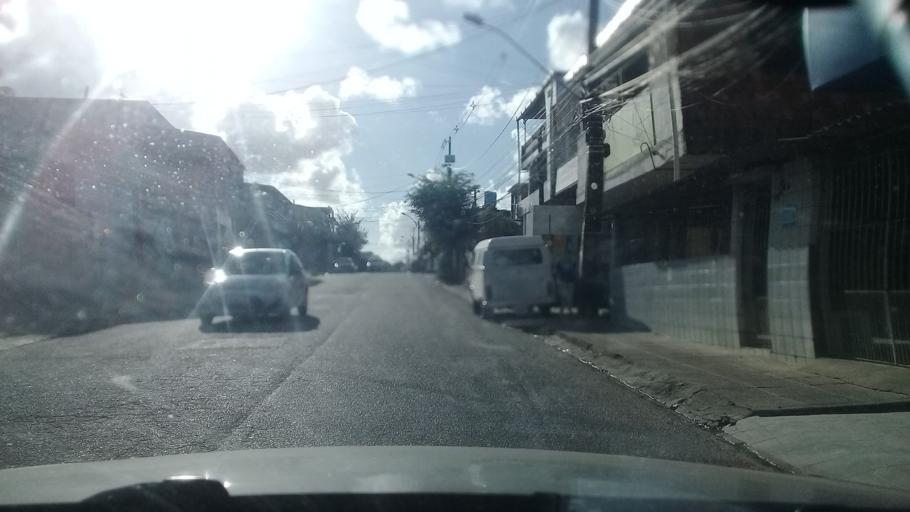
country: BR
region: Pernambuco
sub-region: Jaboatao Dos Guararapes
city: Jaboatao dos Guararapes
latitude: -8.1215
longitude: -34.9365
